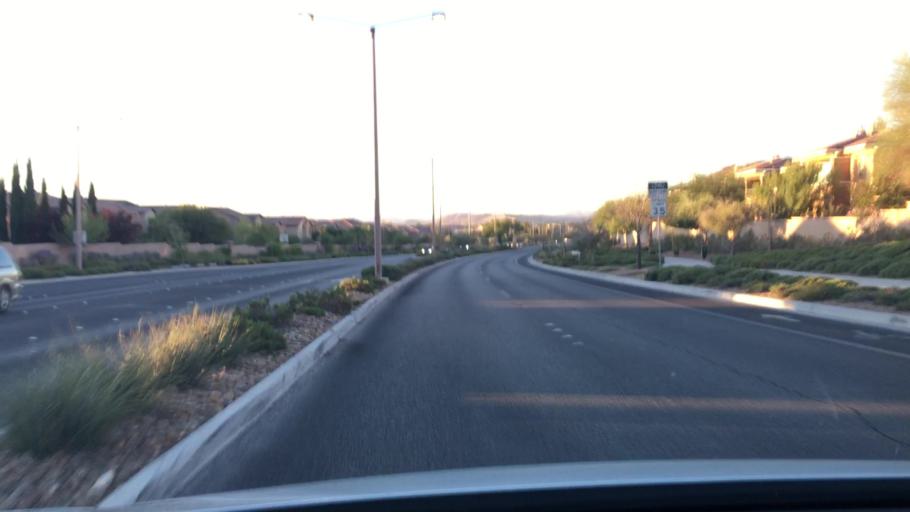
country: US
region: Nevada
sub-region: Clark County
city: Summerlin South
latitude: 36.1640
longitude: -115.3527
